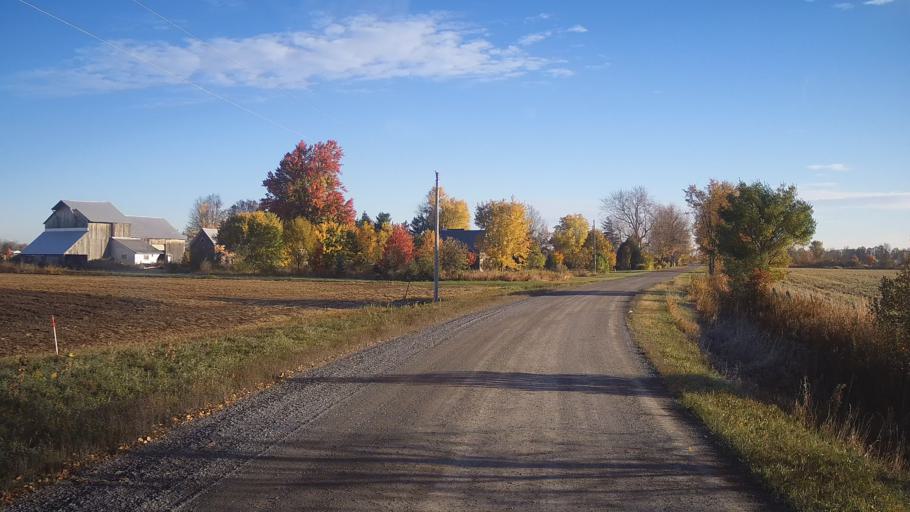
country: CA
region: Ontario
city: Arnprior
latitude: 45.3521
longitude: -76.3103
